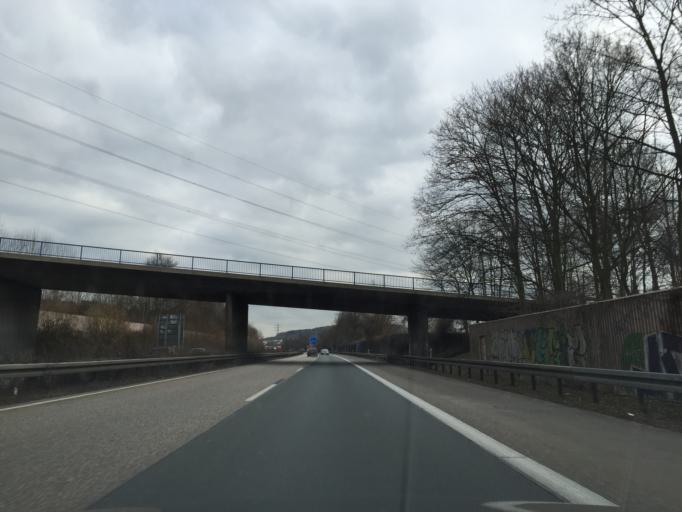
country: DE
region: North Rhine-Westphalia
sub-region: Regierungsbezirk Arnsberg
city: Nachrodt-Wiblingwerde
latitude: 51.3662
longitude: 7.5606
